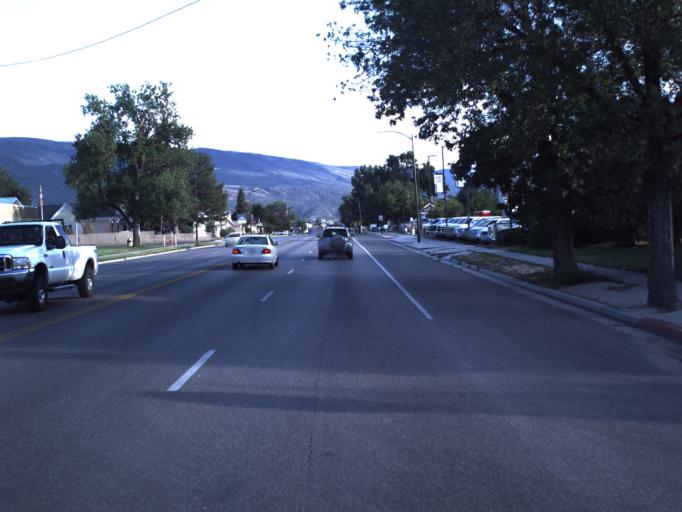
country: US
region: Utah
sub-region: Sanpete County
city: Ephraim
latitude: 39.3580
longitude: -111.5872
